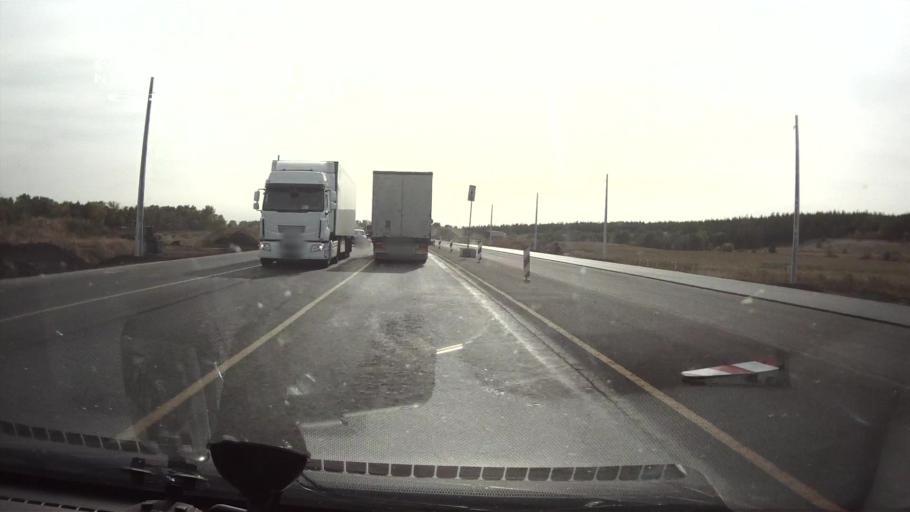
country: RU
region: Saratov
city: Sinodskoye
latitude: 52.0162
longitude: 46.6966
